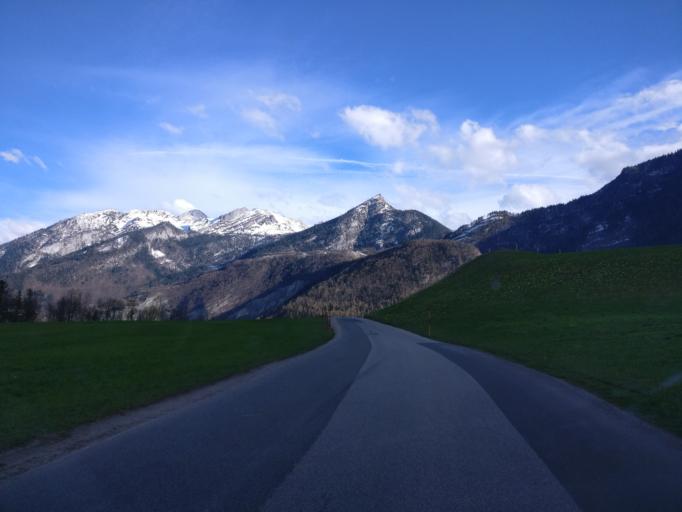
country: AT
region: Salzburg
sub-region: Politischer Bezirk Hallein
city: Golling an der Salzach
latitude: 47.5900
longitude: 13.1586
